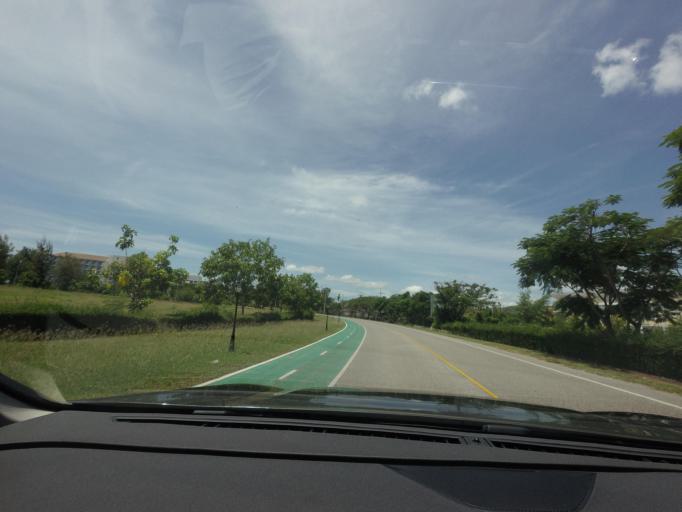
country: TH
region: Prachuap Khiri Khan
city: Hua Hin
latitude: 12.5054
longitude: 99.9728
